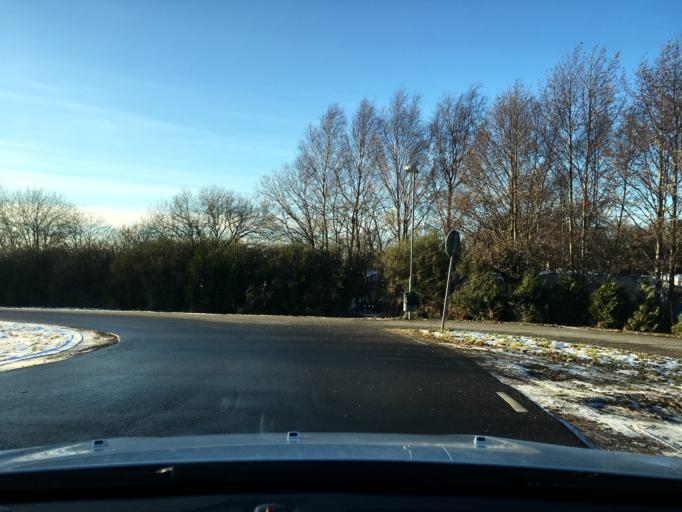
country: SE
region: Vaestra Goetaland
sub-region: Stenungsunds Kommun
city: Stenungsund
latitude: 58.0518
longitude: 11.8180
